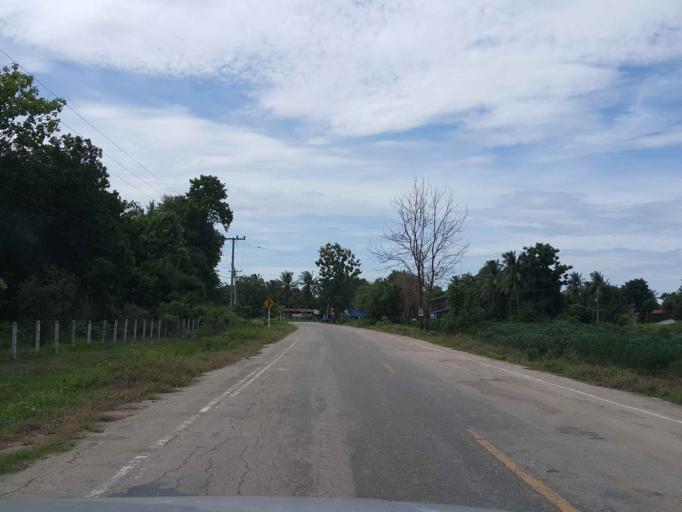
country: TH
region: Sukhothai
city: Ban Dan Lan Hoi
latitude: 17.0790
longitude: 99.4793
